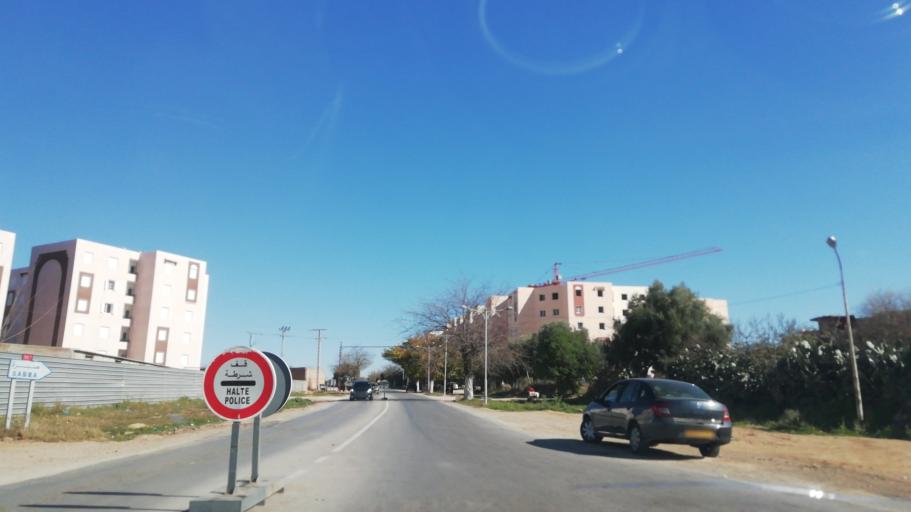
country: DZ
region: Tlemcen
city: Beni Mester
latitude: 34.8240
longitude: -1.5409
